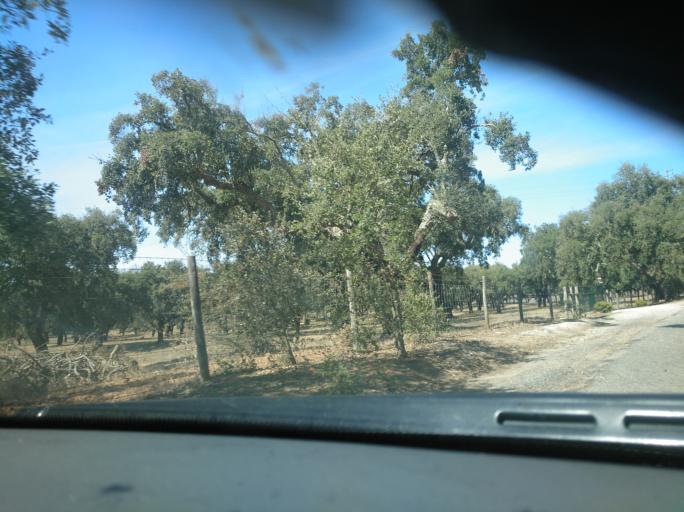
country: PT
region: Evora
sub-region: Arraiolos
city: Arraiolos
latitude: 38.6979
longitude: -8.0941
